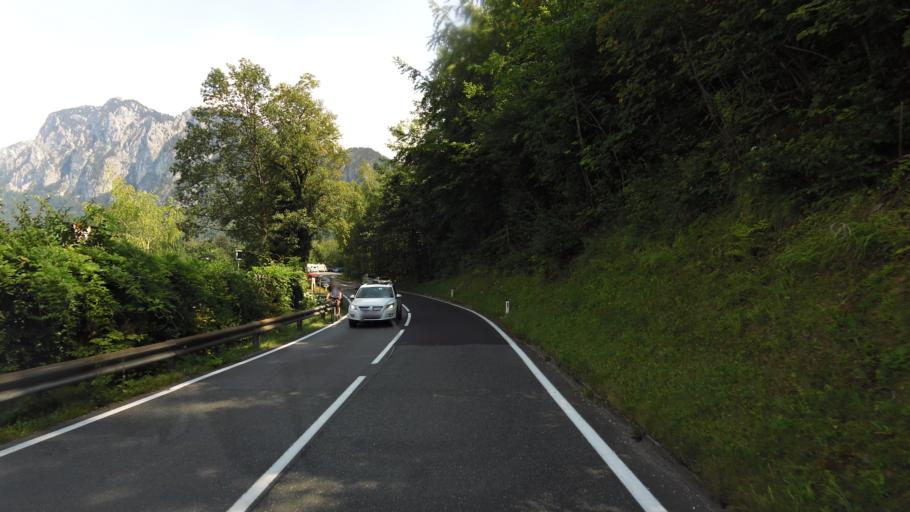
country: AT
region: Upper Austria
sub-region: Politischer Bezirk Vocklabruck
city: Steinbach am Attersee
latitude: 47.7971
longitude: 13.5262
